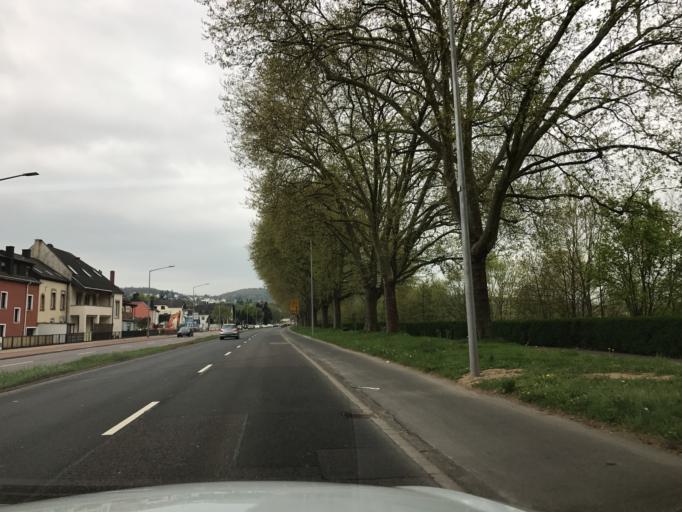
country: DE
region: Rheinland-Pfalz
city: Trier
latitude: 49.7353
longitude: 6.6280
